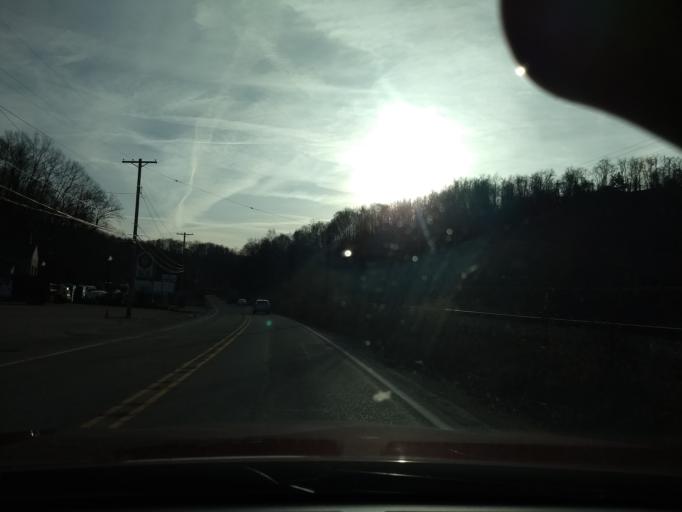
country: US
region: Pennsylvania
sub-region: Allegheny County
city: Brentwood
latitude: 40.3727
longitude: -79.9440
